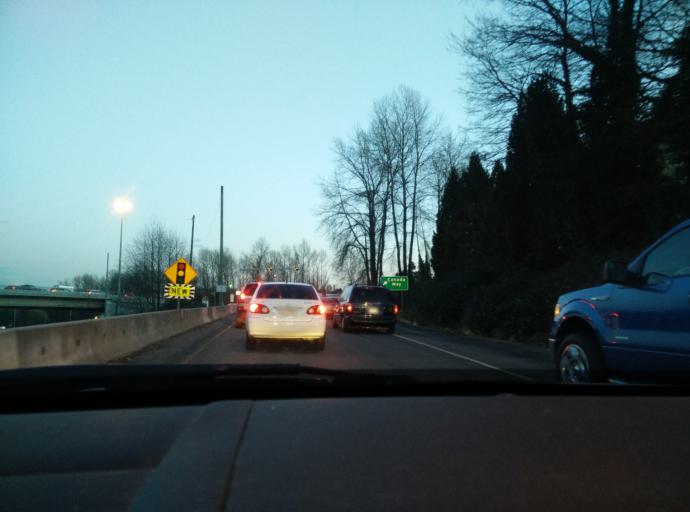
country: CA
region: British Columbia
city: Burnaby
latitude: 49.2444
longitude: -122.9690
